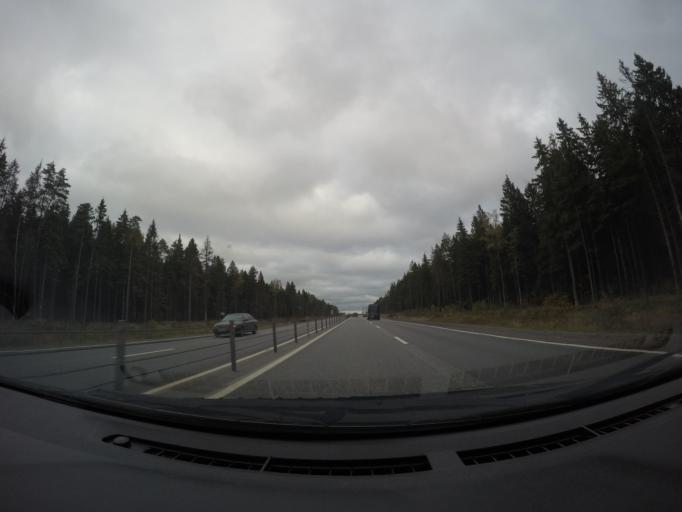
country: RU
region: Moskovskaya
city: Tuchkovo
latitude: 55.5538
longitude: 36.5174
